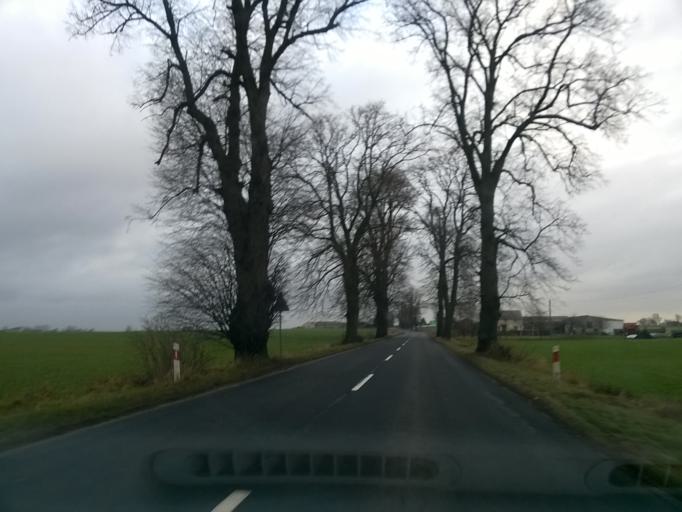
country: PL
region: Greater Poland Voivodeship
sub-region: Powiat wagrowiecki
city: Wapno
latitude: 52.9442
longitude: 17.4029
